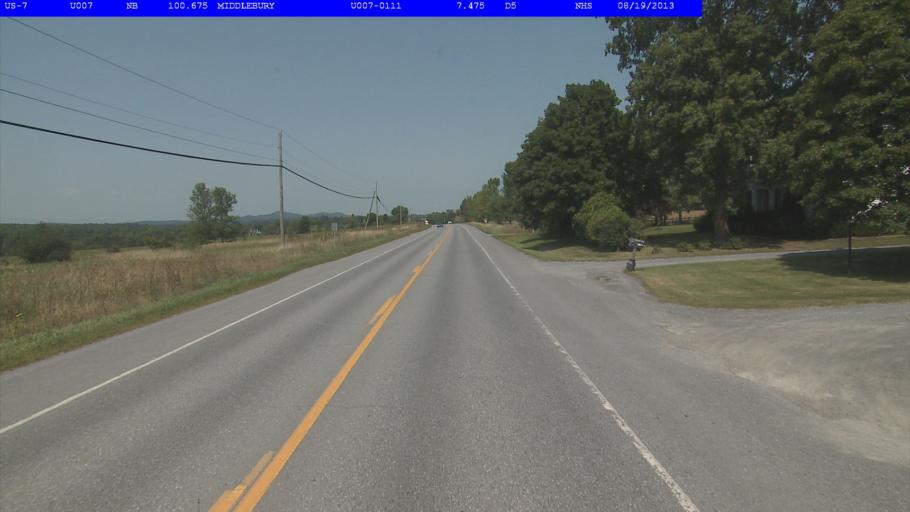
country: US
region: Vermont
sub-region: Addison County
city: Middlebury (village)
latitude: 44.0469
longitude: -73.1635
